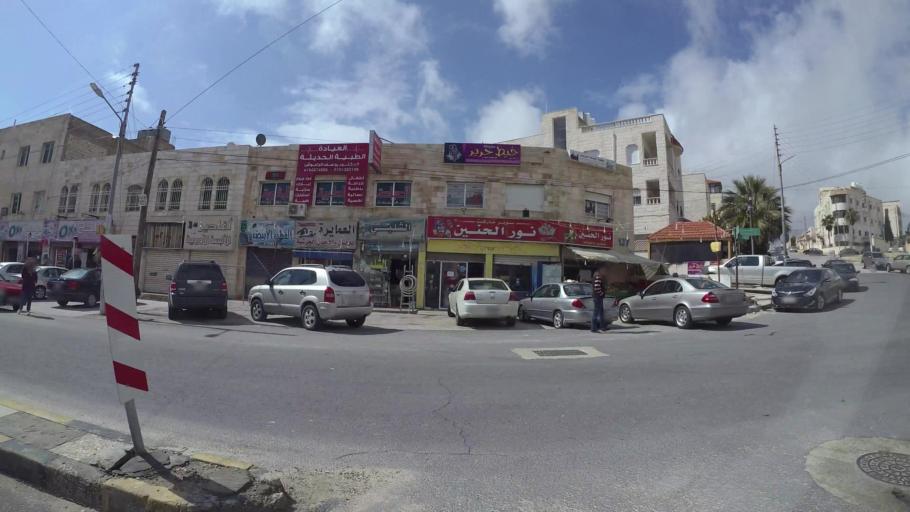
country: JO
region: Amman
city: Al Jubayhah
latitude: 32.0622
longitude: 35.8782
